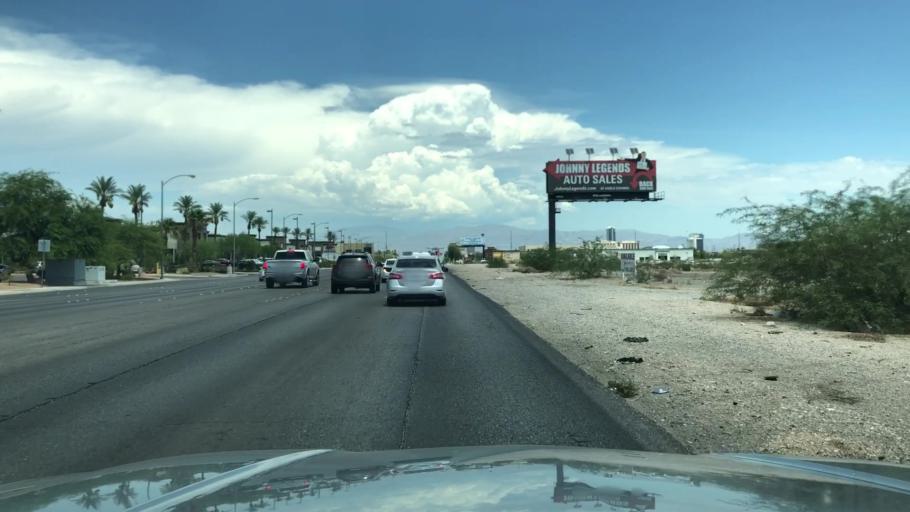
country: US
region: Nevada
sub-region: Clark County
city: Spring Valley
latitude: 36.0791
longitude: -115.2078
